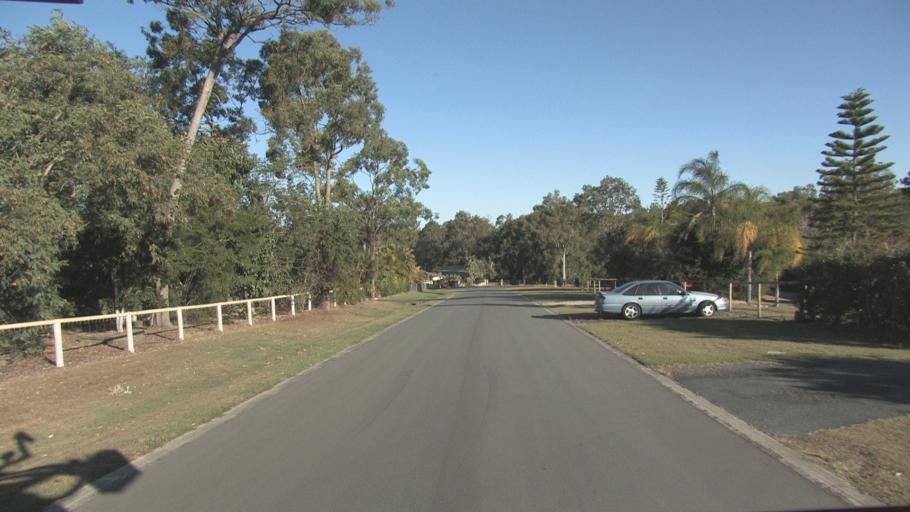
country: AU
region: Queensland
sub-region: Logan
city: North Maclean
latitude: -27.7453
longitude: 152.9657
